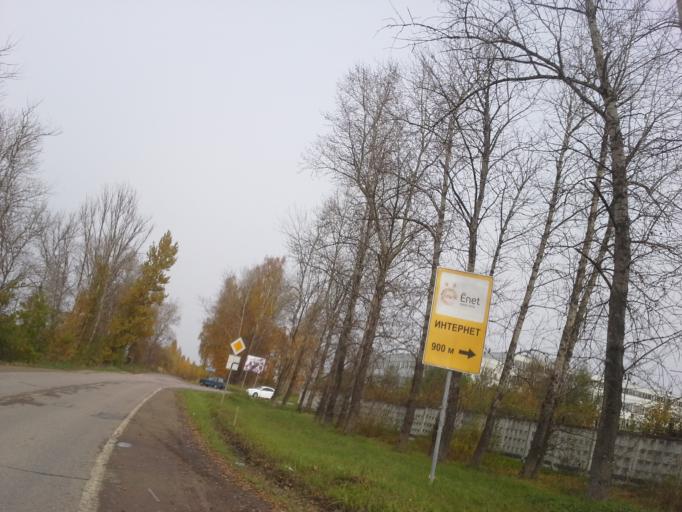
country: RU
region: Moskovskaya
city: Bol'shiye Vyazemy
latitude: 55.6395
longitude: 36.9991
